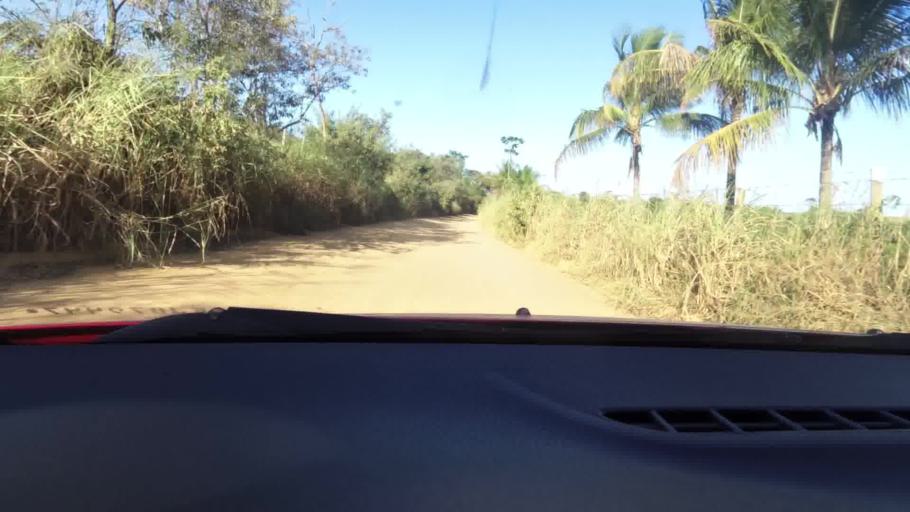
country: BR
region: Espirito Santo
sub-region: Guarapari
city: Guarapari
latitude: -20.5373
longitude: -40.4433
